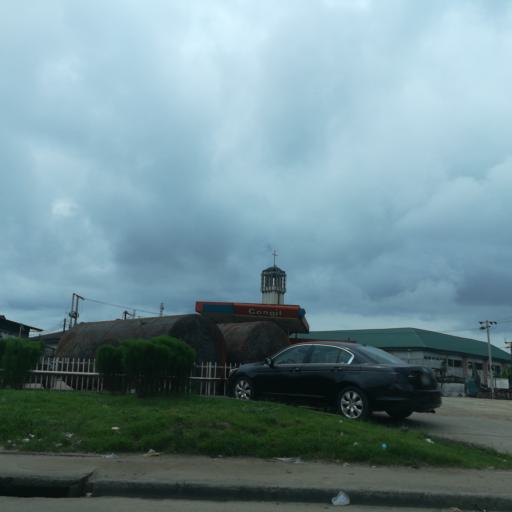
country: NG
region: Rivers
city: Port Harcourt
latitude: 4.7922
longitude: 7.0015
